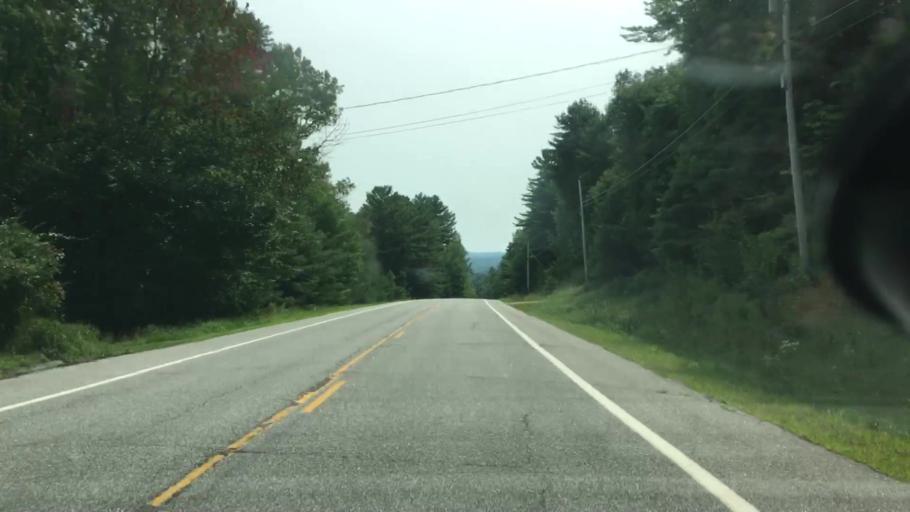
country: US
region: Maine
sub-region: Kennebec County
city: Wayne
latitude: 44.3752
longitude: -70.0974
